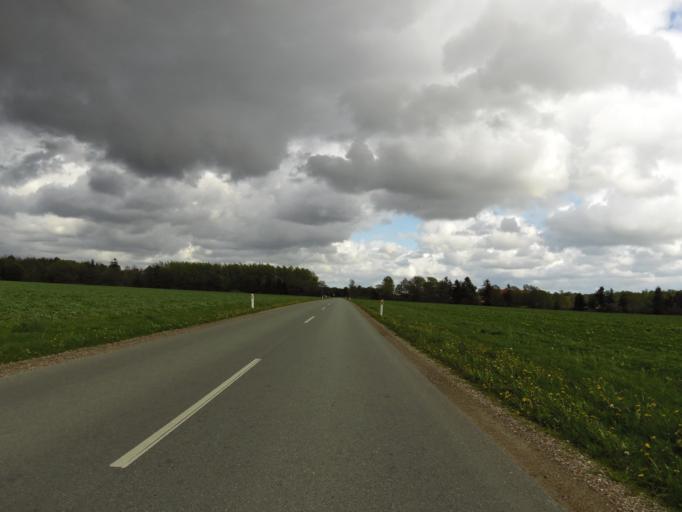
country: DK
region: South Denmark
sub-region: Haderslev Kommune
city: Gram
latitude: 55.2998
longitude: 9.0515
